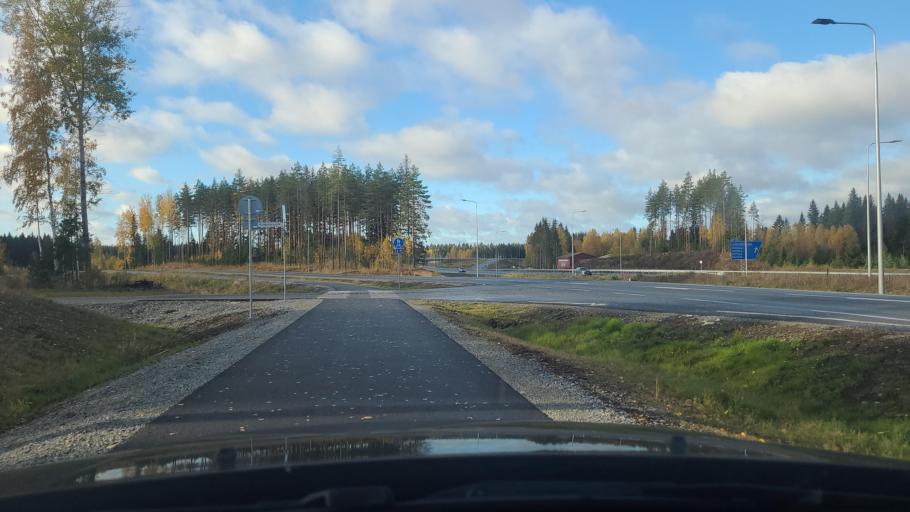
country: FI
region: Southern Savonia
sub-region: Pieksaemaeki
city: Juva
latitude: 61.8804
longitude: 27.7774
